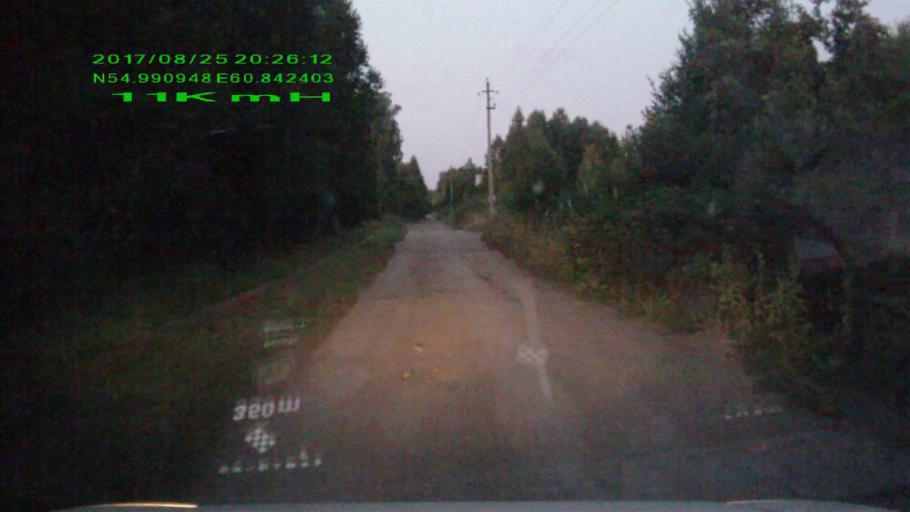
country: RU
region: Chelyabinsk
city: Timiryazevskiy
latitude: 54.9910
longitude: 60.8425
